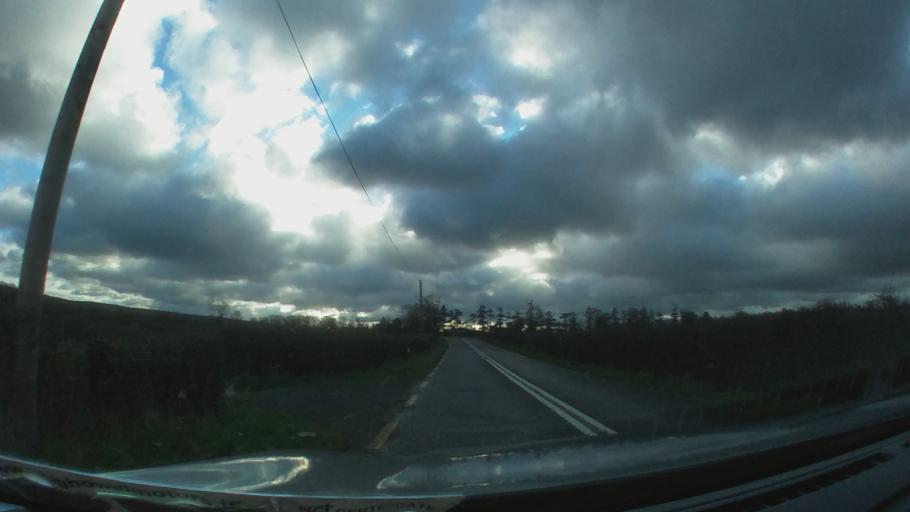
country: IE
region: Leinster
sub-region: Kilkenny
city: Thomastown
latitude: 52.5706
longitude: -7.1153
